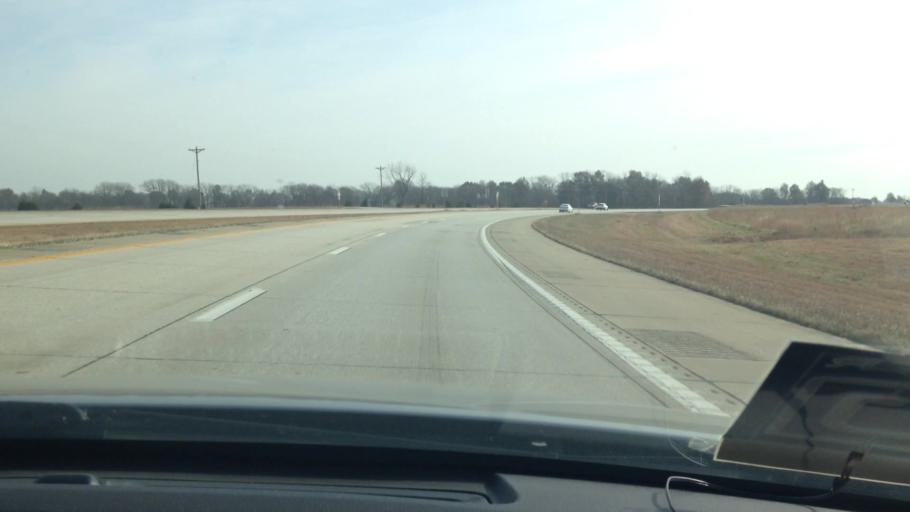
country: US
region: Missouri
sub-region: Henry County
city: Clinton
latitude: 38.4632
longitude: -93.9720
